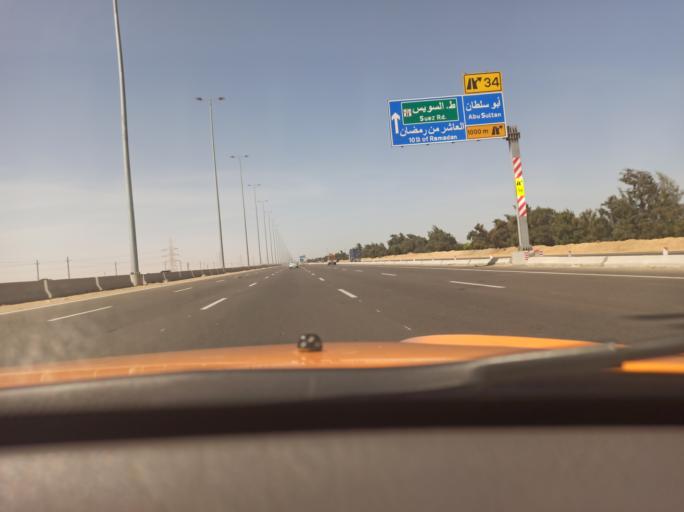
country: EG
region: Al Isma'iliyah
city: At Tall al Kabir
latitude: 30.4219
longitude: 32.0287
